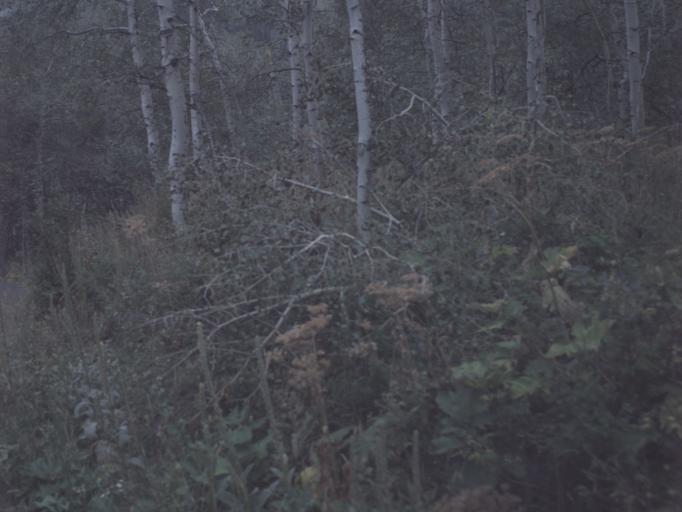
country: US
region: Utah
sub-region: Utah County
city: Lindon
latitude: 40.4210
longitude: -111.6049
